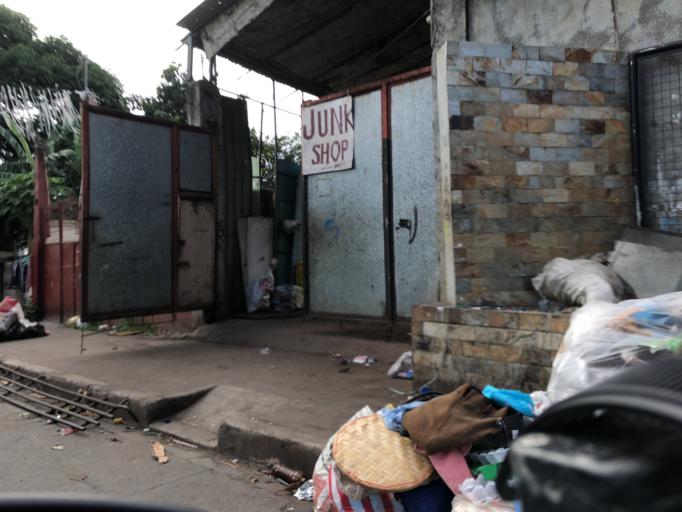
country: PH
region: Central Luzon
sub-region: Province of Bulacan
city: San Jose del Monte
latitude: 14.7420
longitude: 121.0608
